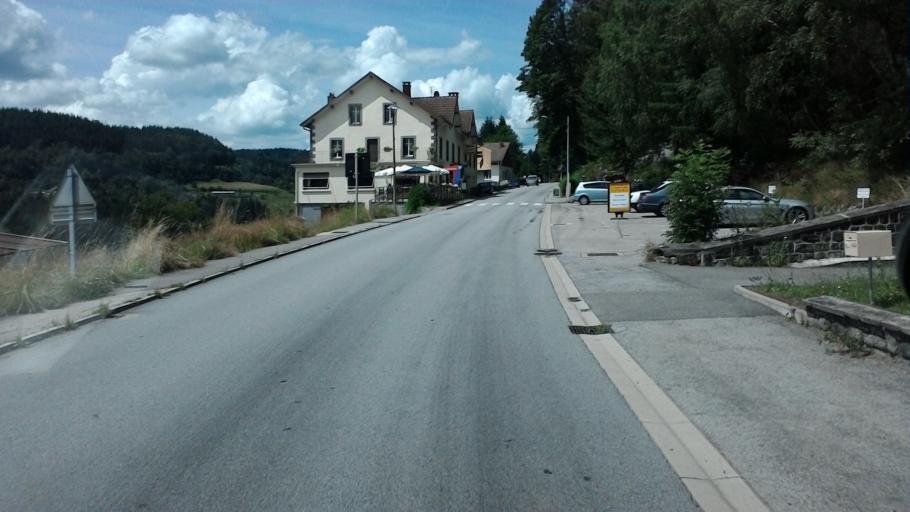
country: FR
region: Lorraine
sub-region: Departement des Vosges
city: Le Tholy
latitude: 48.0832
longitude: 6.7404
